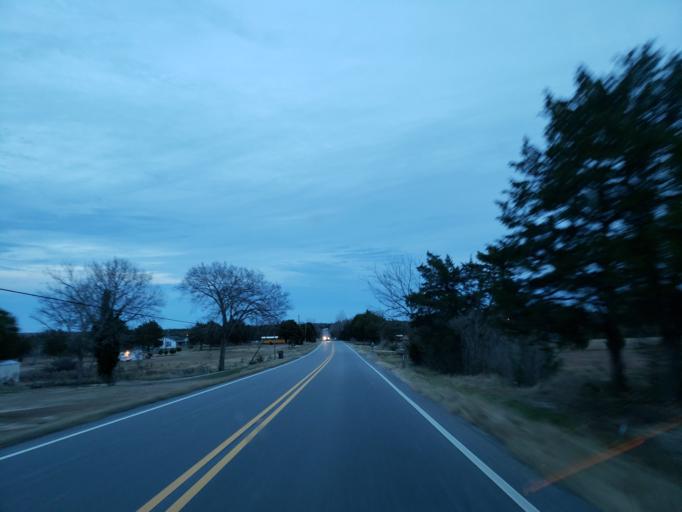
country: US
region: Alabama
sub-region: Sumter County
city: Livingston
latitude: 32.8098
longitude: -88.2293
